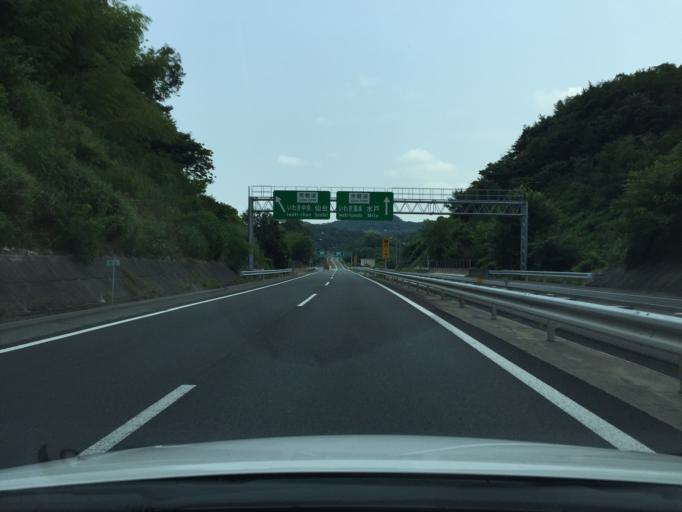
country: JP
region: Fukushima
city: Iwaki
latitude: 37.0408
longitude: 140.8128
